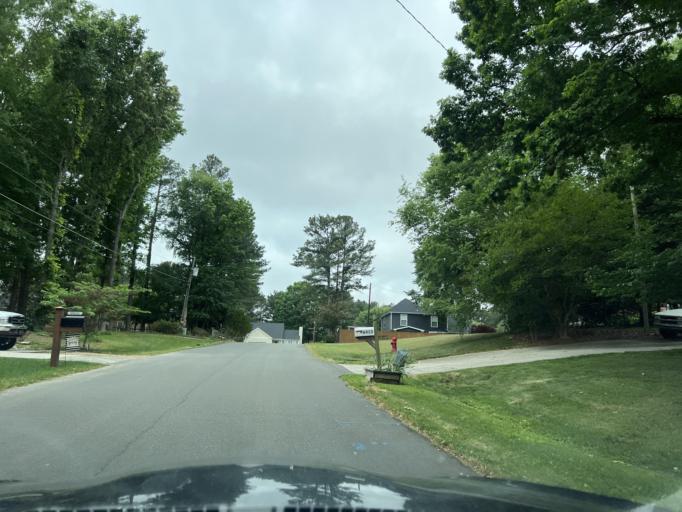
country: US
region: North Carolina
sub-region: Wake County
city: Knightdale
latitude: 35.8666
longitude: -78.5481
